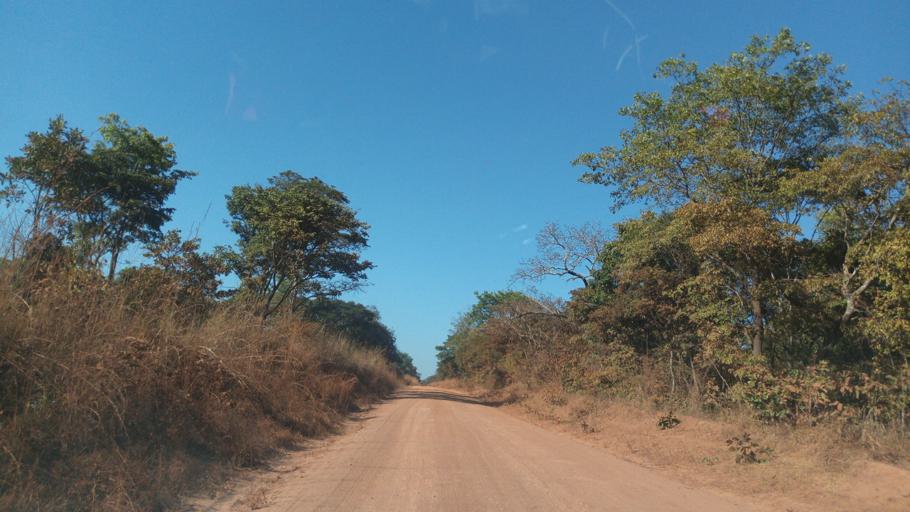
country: ZM
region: Luapula
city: Mwense
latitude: -10.6367
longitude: 28.4092
